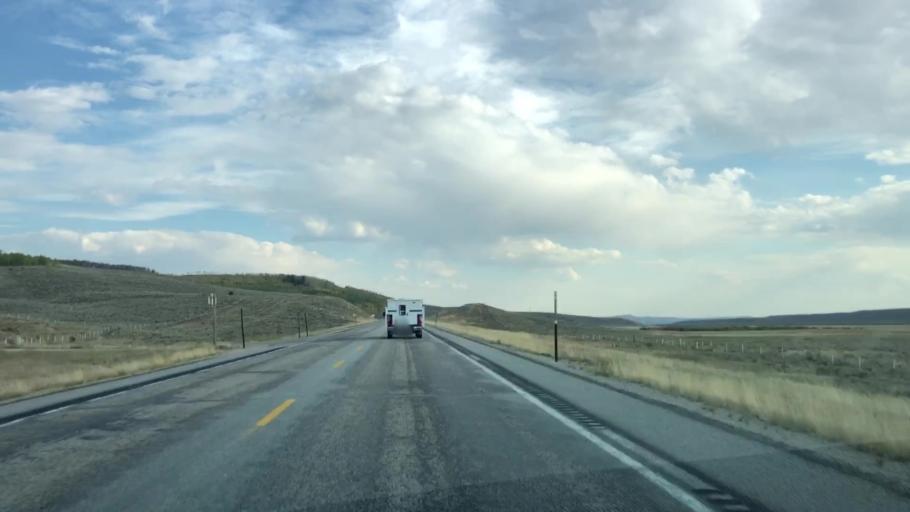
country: US
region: Wyoming
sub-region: Sublette County
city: Pinedale
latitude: 43.0954
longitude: -110.1669
